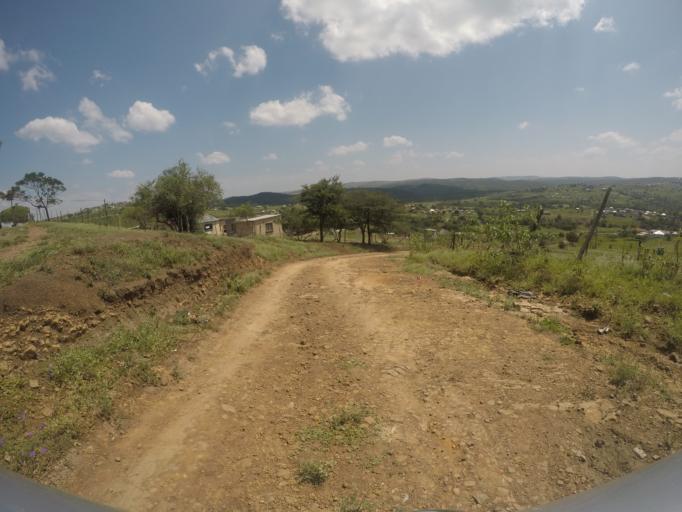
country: ZA
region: KwaZulu-Natal
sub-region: uThungulu District Municipality
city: Empangeni
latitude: -28.5977
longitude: 31.7385
